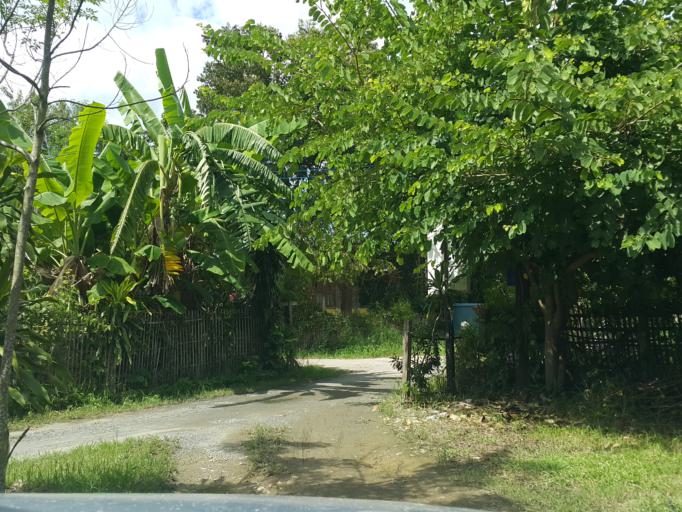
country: TH
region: Chiang Mai
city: San Kamphaeng
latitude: 18.7533
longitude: 99.1253
